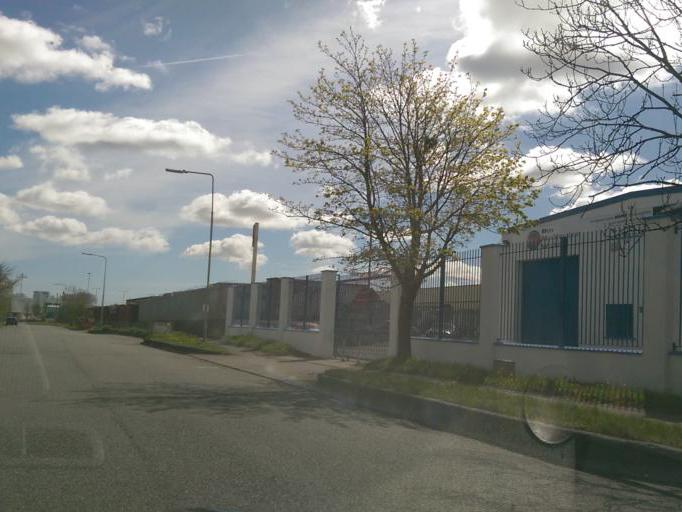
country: IE
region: Leinster
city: Ballyfermot
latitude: 53.3244
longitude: -6.3593
